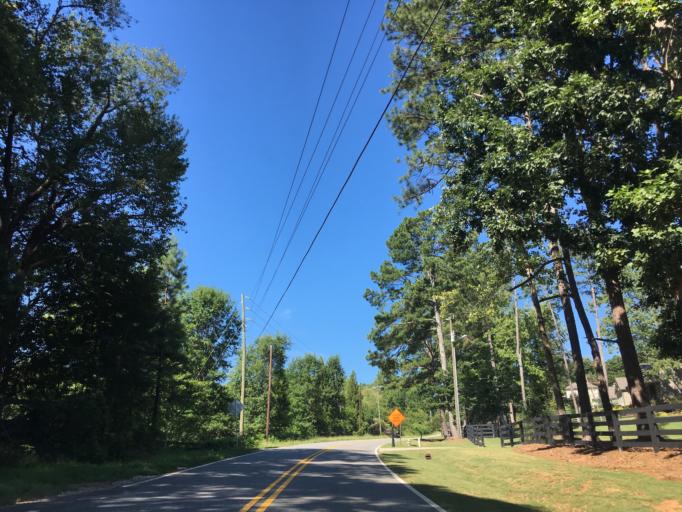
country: US
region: Georgia
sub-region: Fulton County
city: Milton
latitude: 34.1852
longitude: -84.3002
